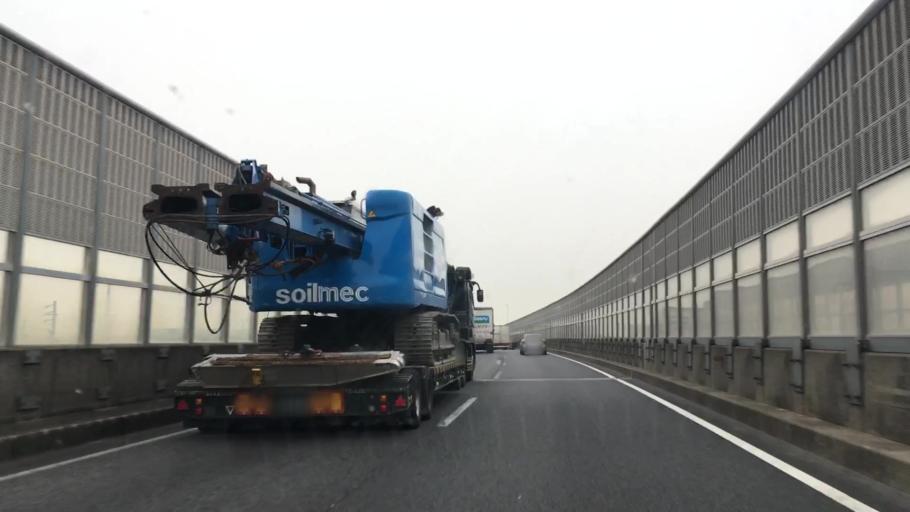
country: JP
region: Aichi
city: Chiryu
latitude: 34.9709
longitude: 137.0342
